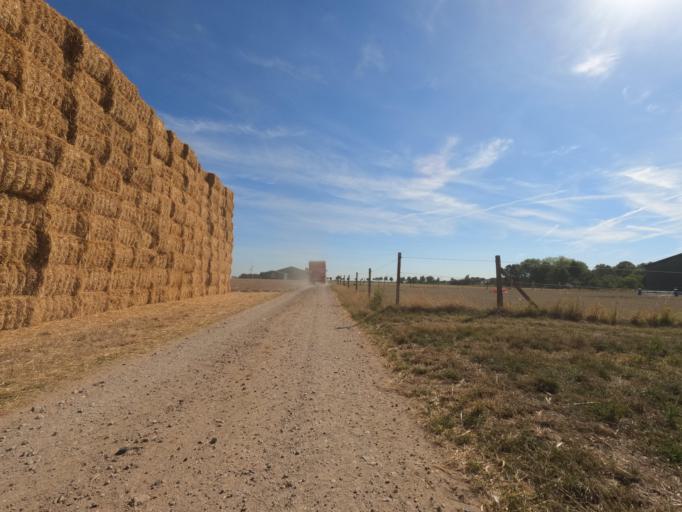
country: DE
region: North Rhine-Westphalia
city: Erkelenz
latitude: 51.0381
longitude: 6.3511
